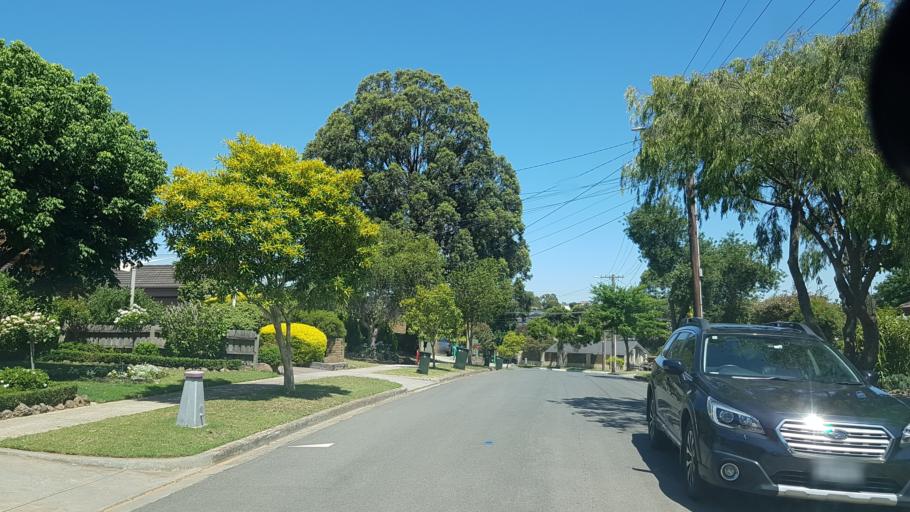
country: AU
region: Victoria
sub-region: Manningham
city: Bulleen
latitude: -37.7578
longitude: 145.0950
